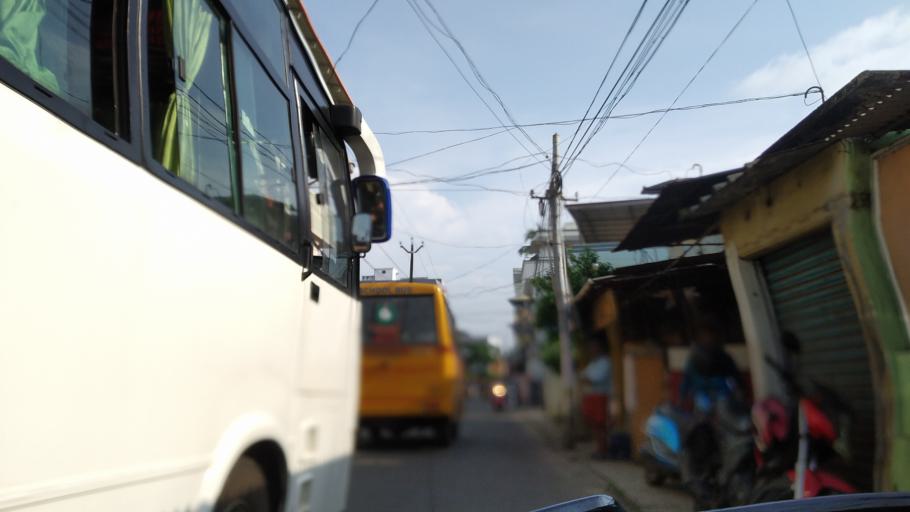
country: IN
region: Kerala
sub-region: Ernakulam
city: Cochin
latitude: 9.9980
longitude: 76.2853
